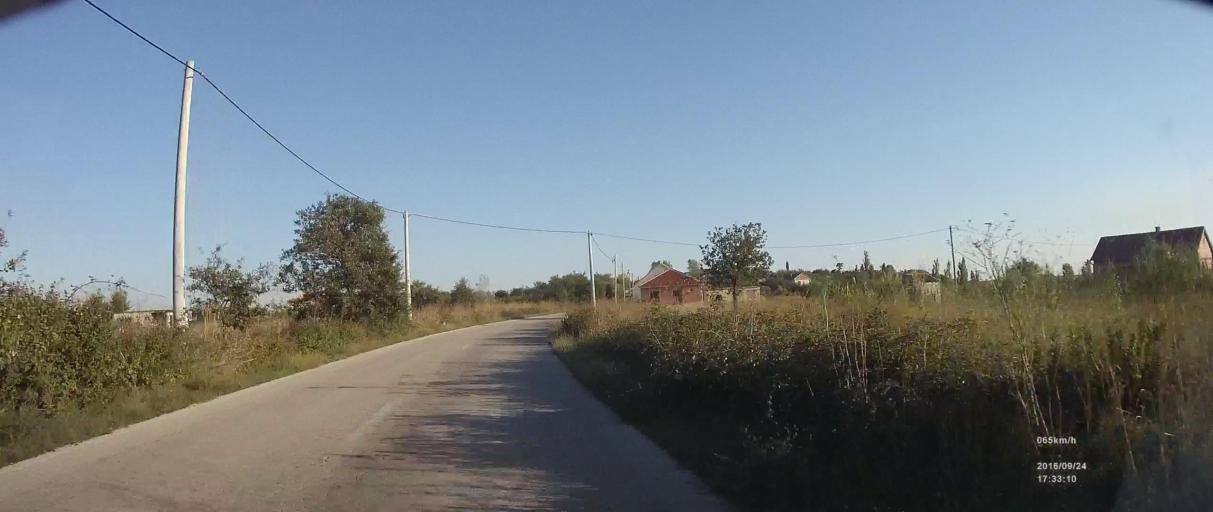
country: HR
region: Zadarska
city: Posedarje
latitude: 44.1767
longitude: 15.4557
